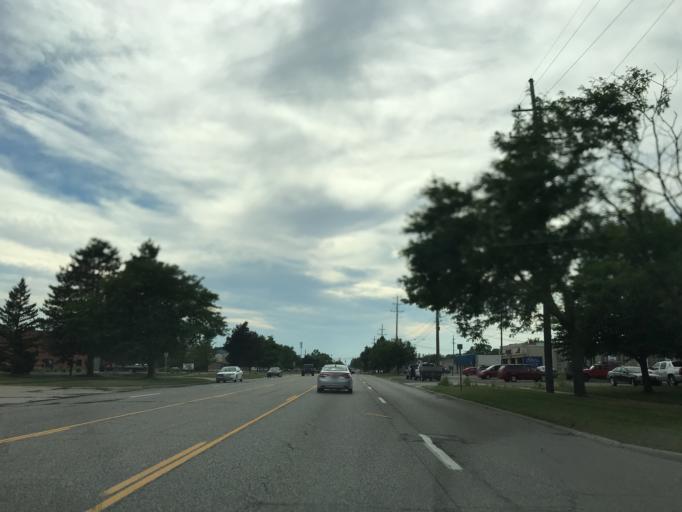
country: US
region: Michigan
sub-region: Oakland County
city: Farmington
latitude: 42.4412
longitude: -83.3522
